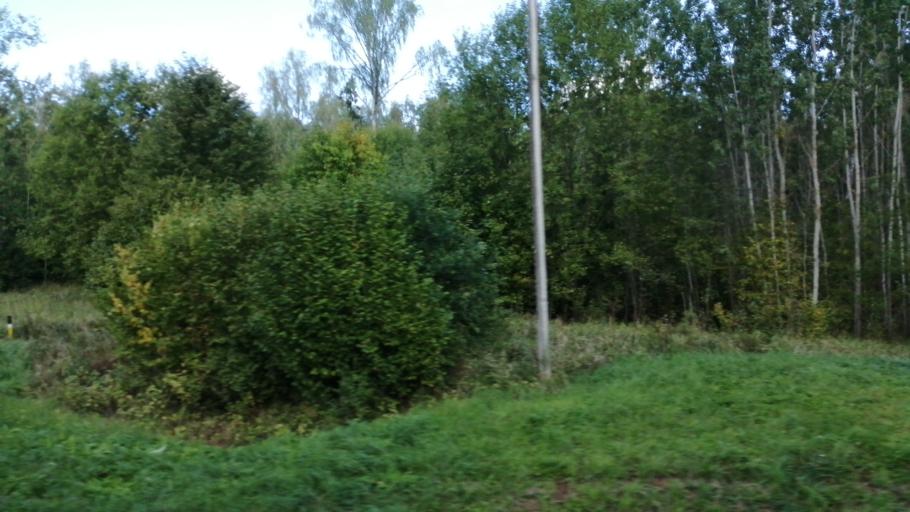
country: EE
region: Tartu
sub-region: Noo vald
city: Noo
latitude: 58.4163
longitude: 26.5536
